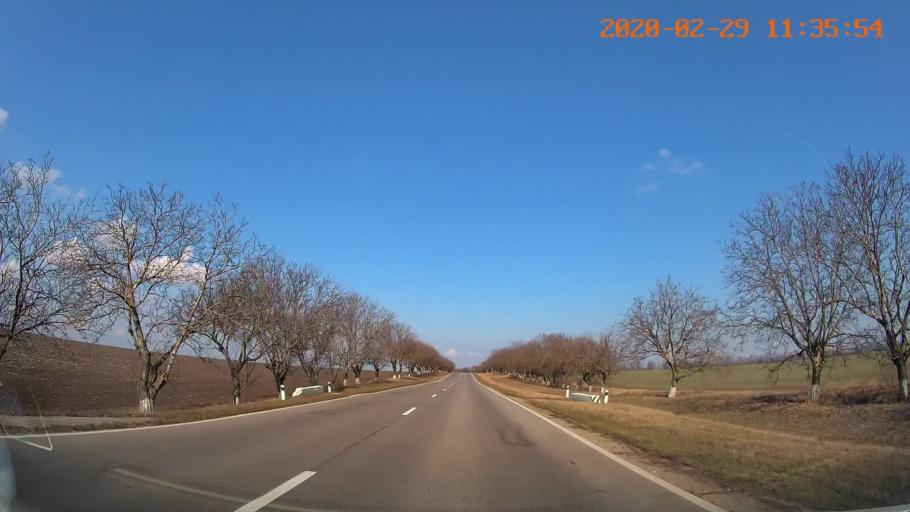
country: MD
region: Rezina
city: Saharna
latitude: 47.5876
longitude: 29.0602
